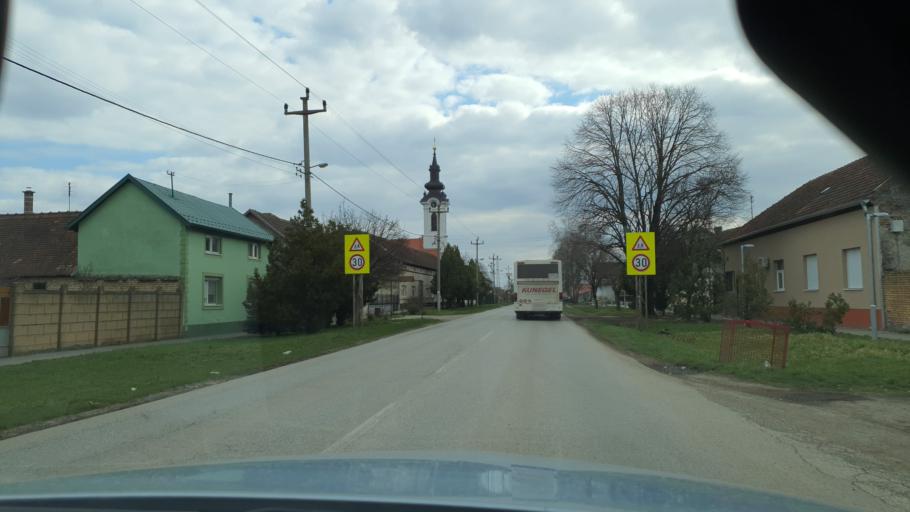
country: RS
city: Obrovac
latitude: 45.4157
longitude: 19.4029
